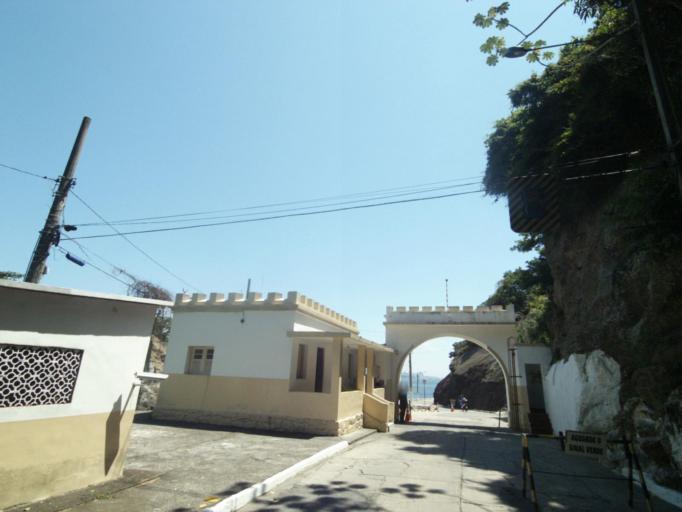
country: BR
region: Rio de Janeiro
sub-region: Niteroi
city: Niteroi
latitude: -22.9336
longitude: -43.1261
